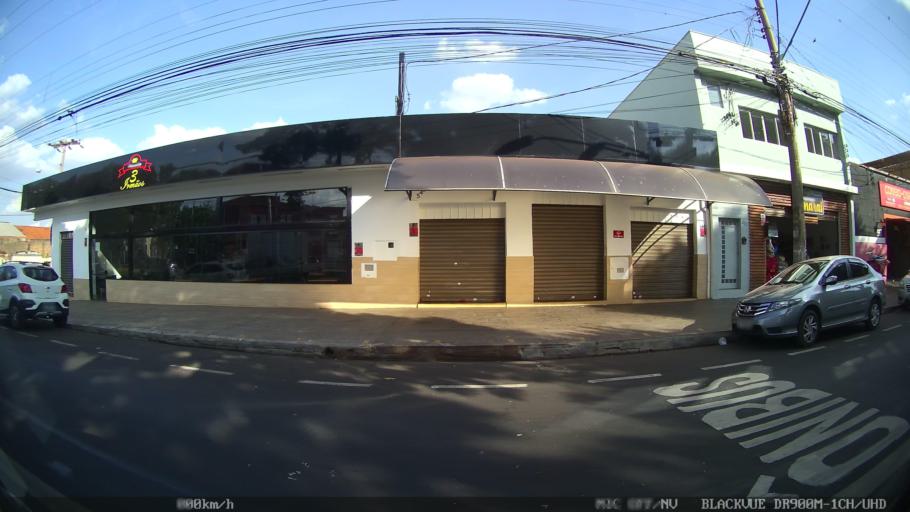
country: BR
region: Sao Paulo
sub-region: Ribeirao Preto
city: Ribeirao Preto
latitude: -21.1752
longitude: -47.8228
